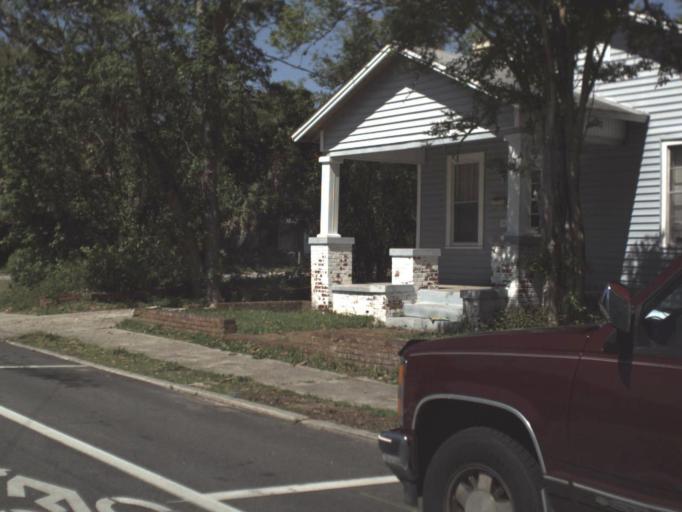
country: US
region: Florida
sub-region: Escambia County
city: Pensacola
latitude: 30.4259
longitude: -87.2115
